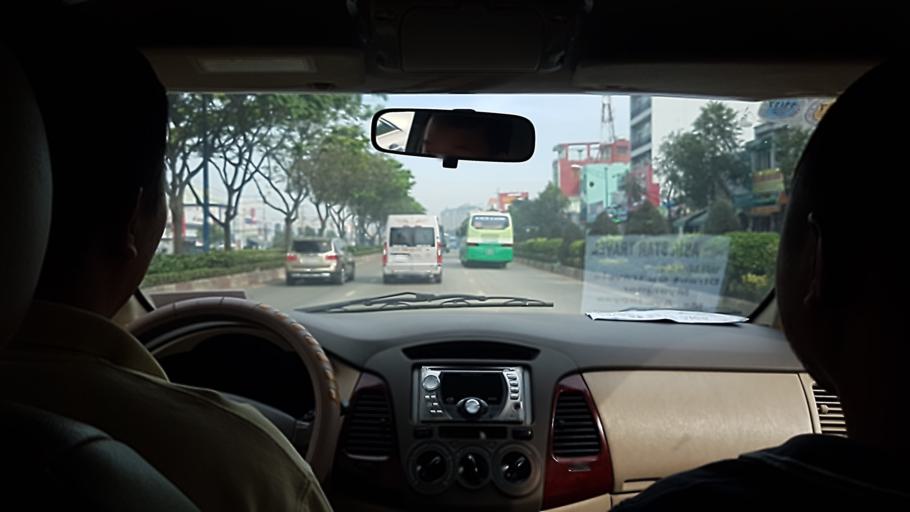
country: VN
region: Ho Chi Minh City
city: Ho Chi Minh City
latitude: 10.8167
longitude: 106.6320
